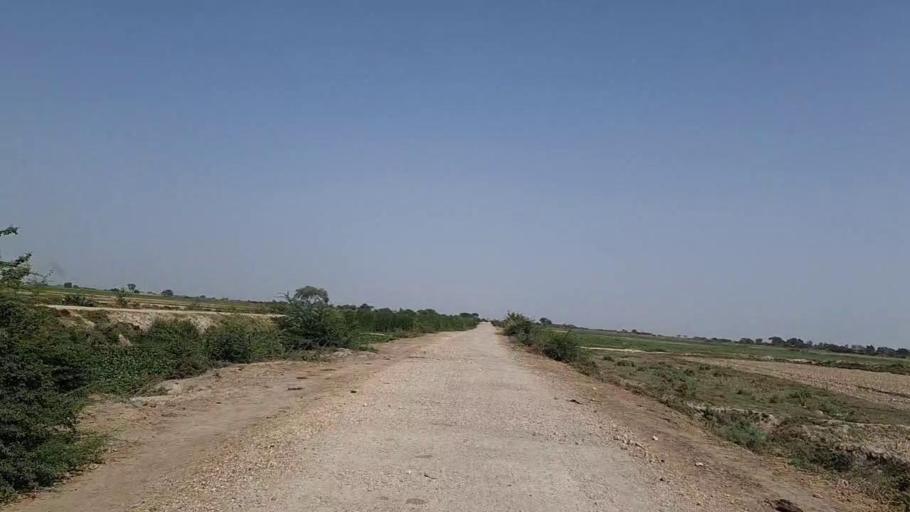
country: PK
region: Sindh
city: Jati
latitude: 24.3607
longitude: 68.2760
